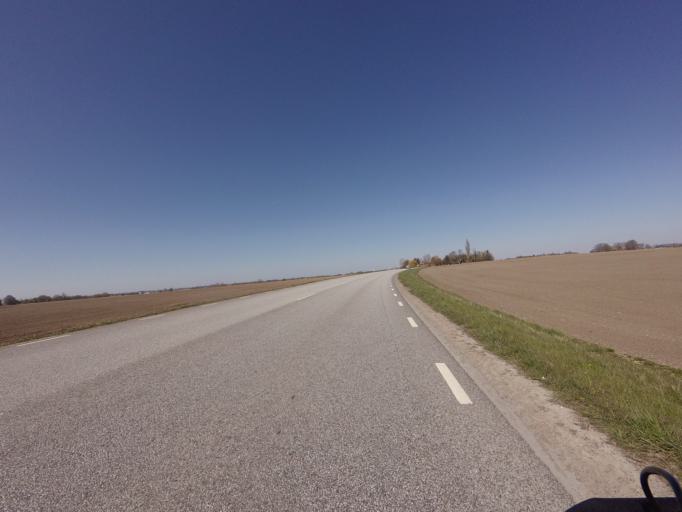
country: SE
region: Skane
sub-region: Vellinge Kommun
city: Vellinge
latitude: 55.4664
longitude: 13.0575
